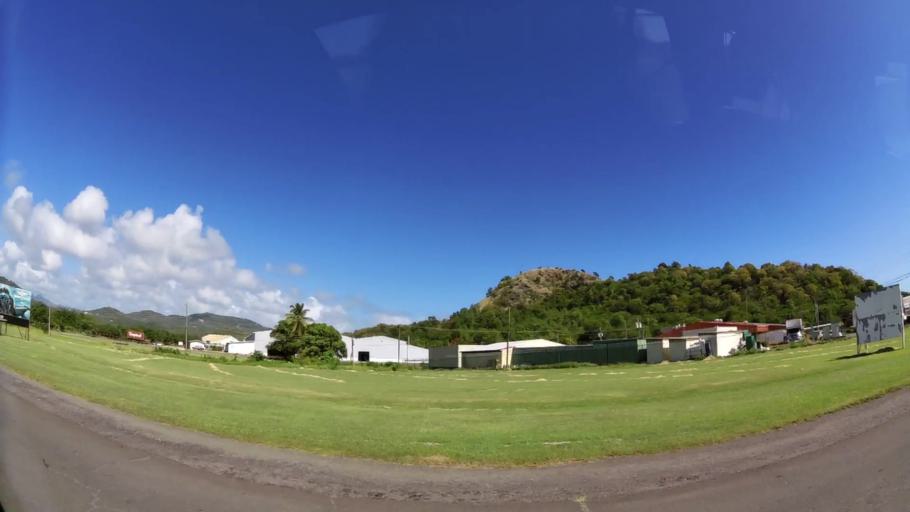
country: LC
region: Vieux-Fort
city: Vieux Fort
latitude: 13.7376
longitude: -60.9476
